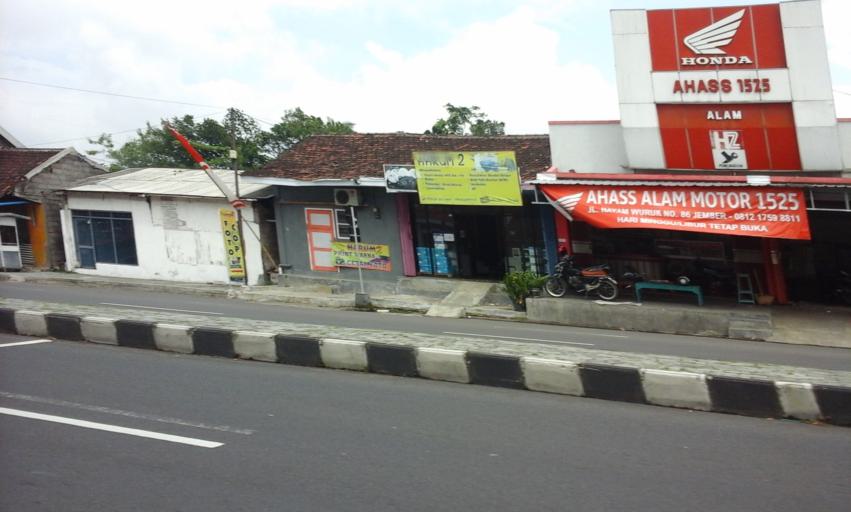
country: ID
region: East Java
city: Krajan
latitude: -8.1865
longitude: 113.6613
